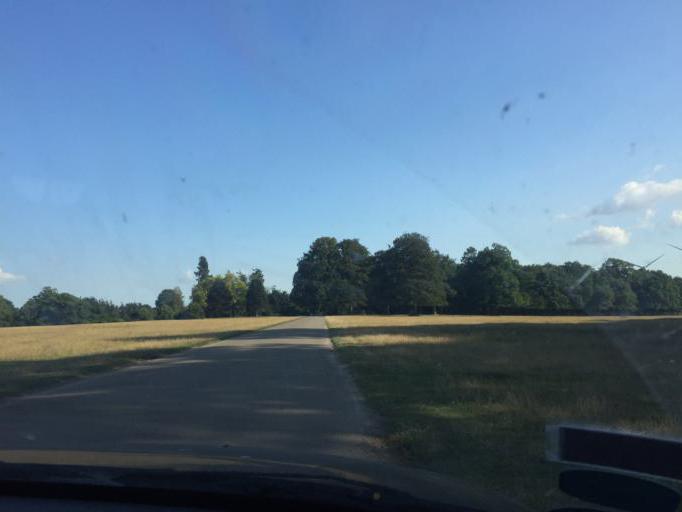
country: DK
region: Zealand
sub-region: Lolland Kommune
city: Maribo
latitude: 54.8252
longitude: 11.5018
